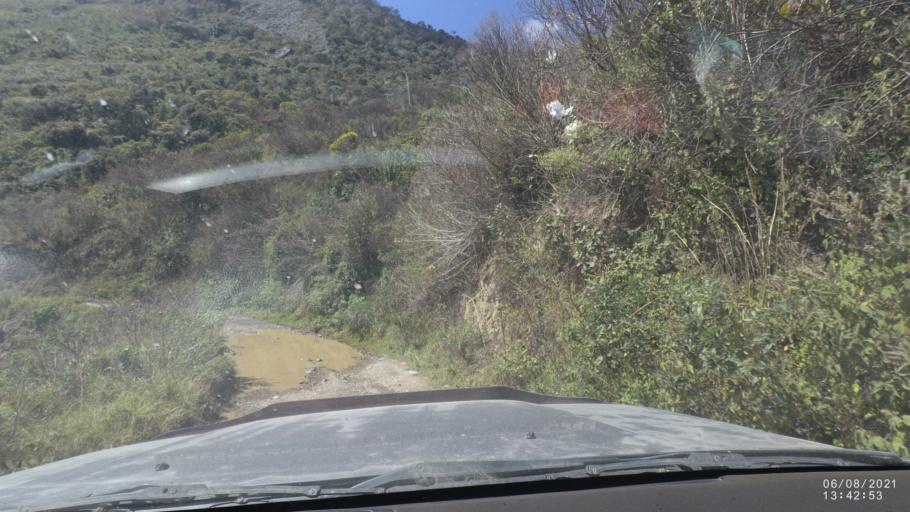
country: BO
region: La Paz
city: Quime
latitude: -16.6789
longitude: -66.7285
